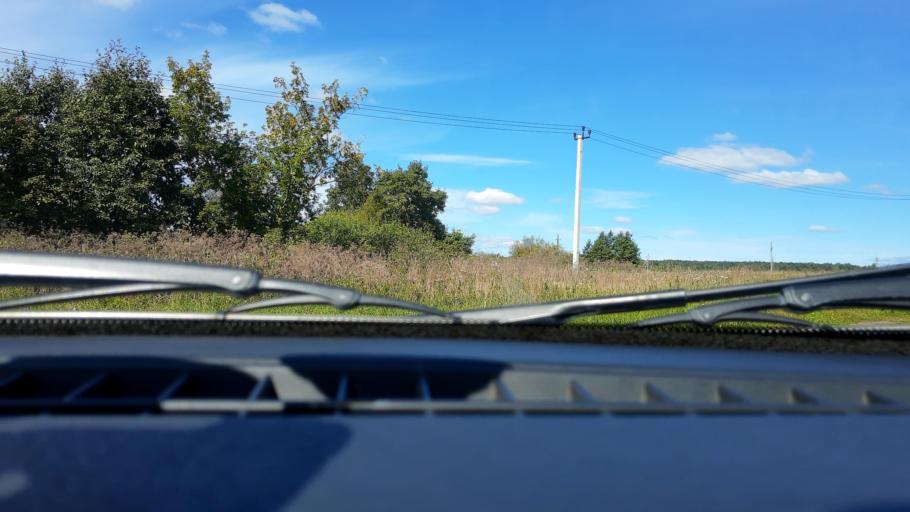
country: RU
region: Bashkortostan
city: Mikhaylovka
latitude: 54.8204
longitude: 55.7900
